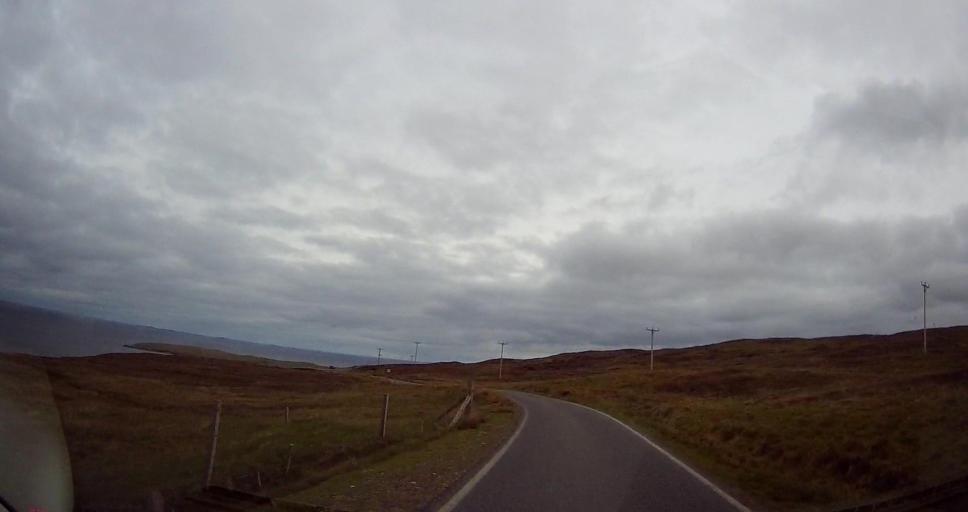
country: GB
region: Scotland
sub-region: Shetland Islands
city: Shetland
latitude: 60.5449
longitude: -1.0555
